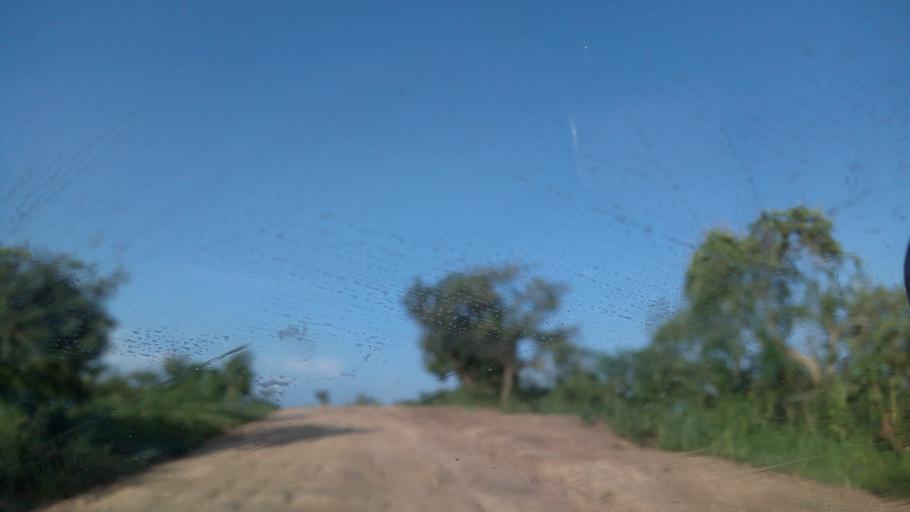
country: BI
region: Bururi
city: Rumonge
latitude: -4.2056
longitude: 29.0159
